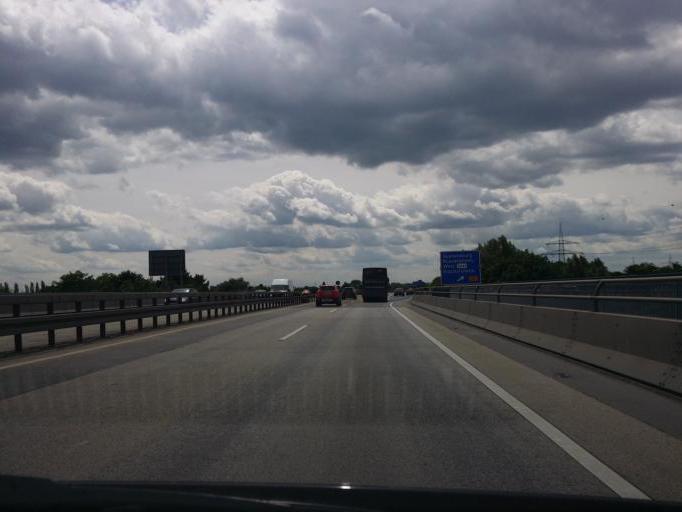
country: DE
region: Hesse
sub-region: Regierungsbezirk Darmstadt
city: Hochheim am Main
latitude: 49.9990
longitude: 8.3454
